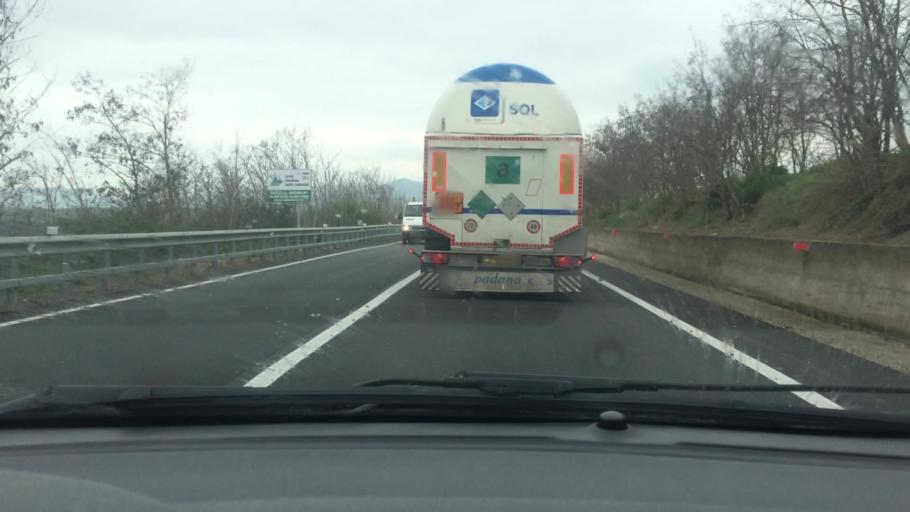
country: IT
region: Basilicate
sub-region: Provincia di Matera
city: Matera
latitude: 40.6197
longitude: 16.5831
